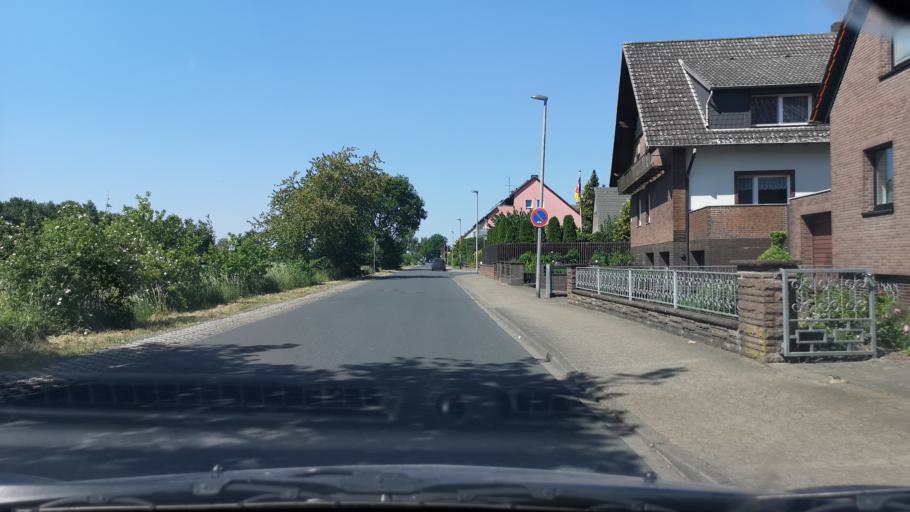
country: DE
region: Lower Saxony
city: Garbsen-Mitte
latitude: 52.4477
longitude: 9.6147
